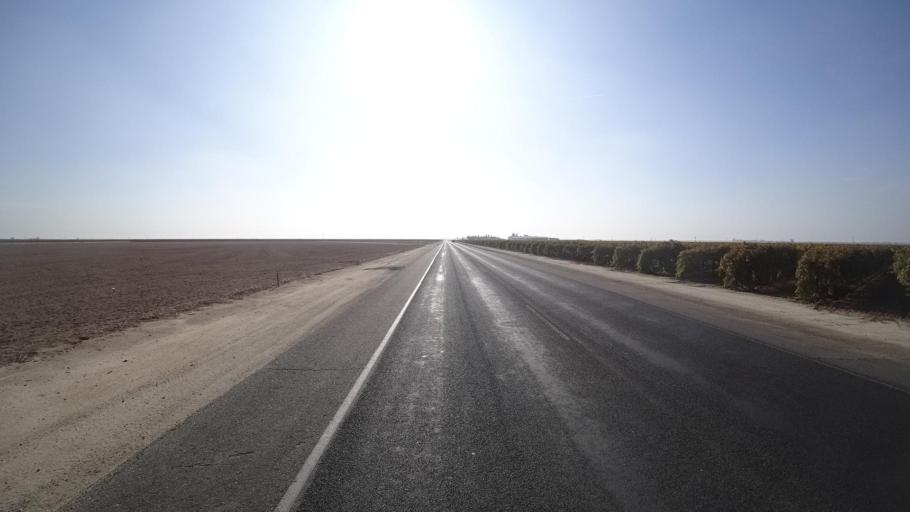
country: US
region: California
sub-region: Kern County
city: McFarland
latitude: 35.6854
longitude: -119.1797
